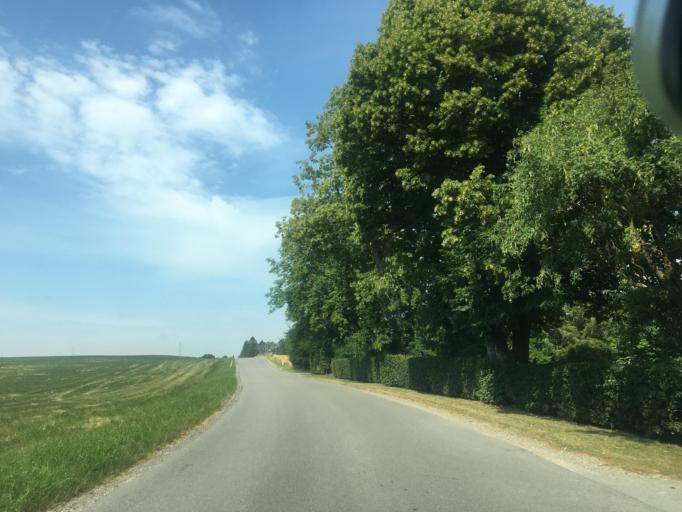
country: DK
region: Zealand
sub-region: Faxe Kommune
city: Ronnede
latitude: 55.2047
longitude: 12.0239
